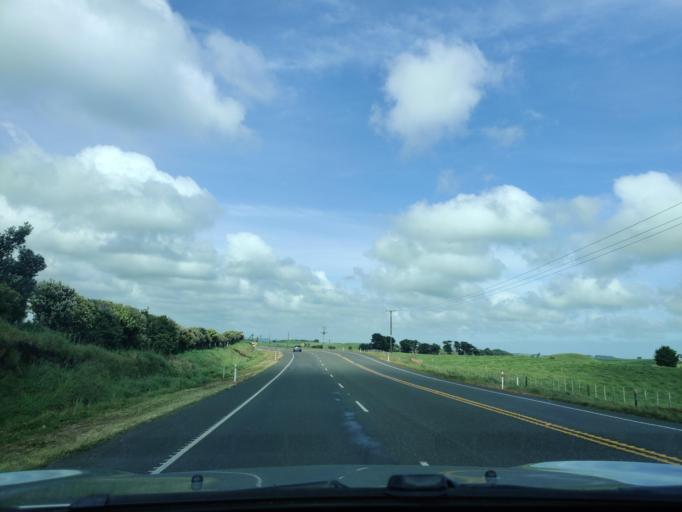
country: NZ
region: Taranaki
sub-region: South Taranaki District
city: Patea
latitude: -39.7682
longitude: 174.6559
